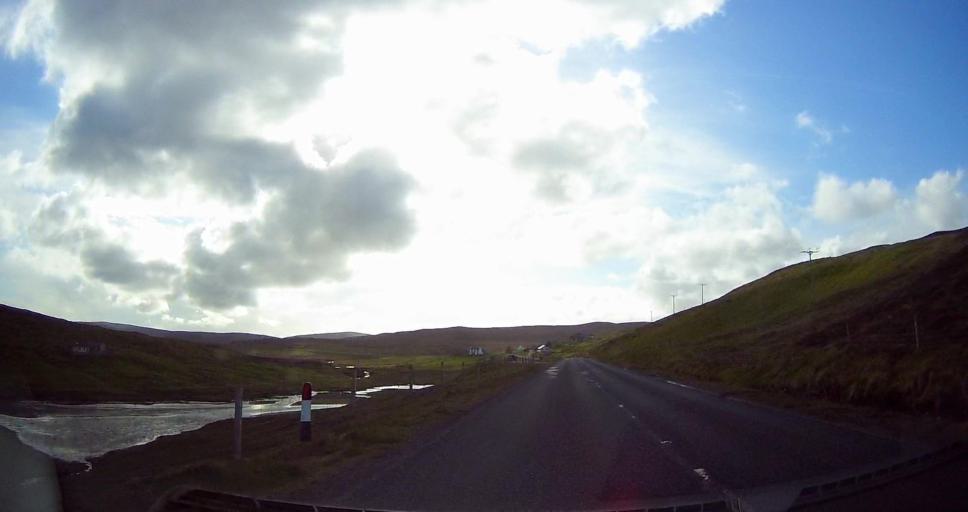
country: GB
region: Scotland
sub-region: Shetland Islands
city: Lerwick
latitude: 60.3530
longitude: -1.1842
